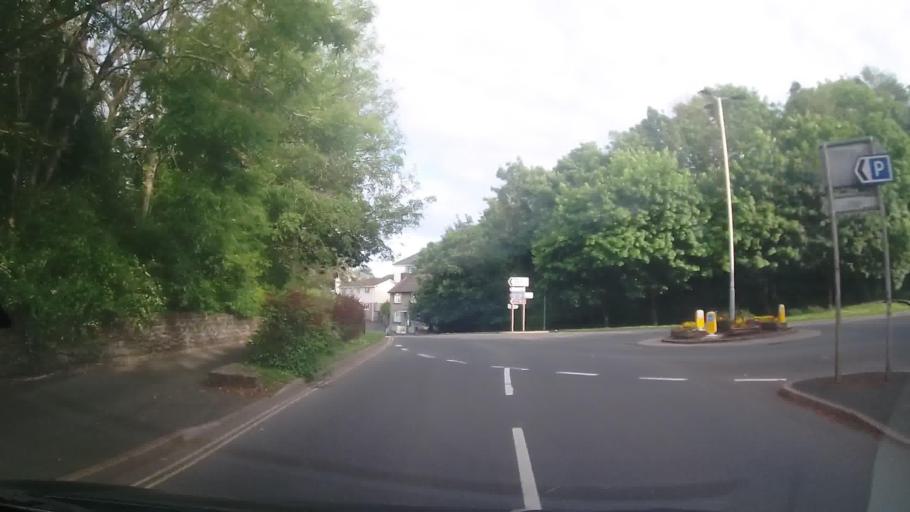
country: GB
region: England
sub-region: Devon
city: Kingsbridge
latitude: 50.2833
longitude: -3.7797
